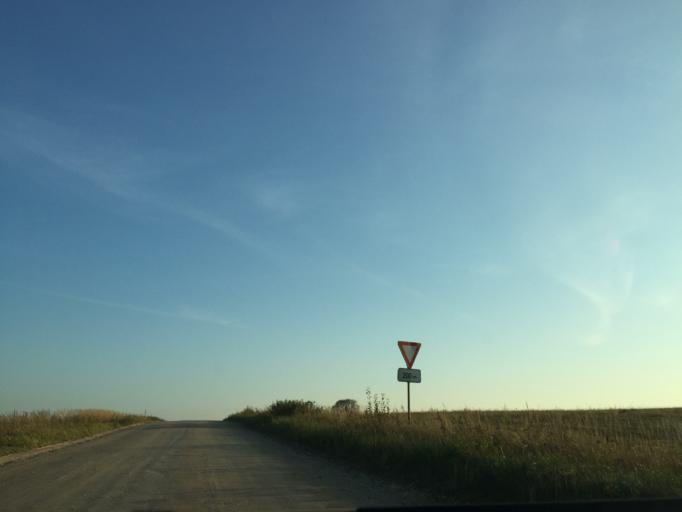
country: LV
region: Vainode
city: Vainode
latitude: 56.5698
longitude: 21.8469
